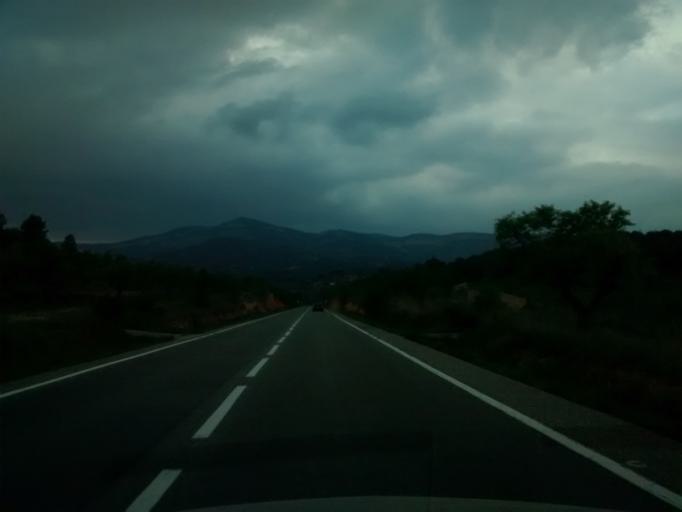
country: ES
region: Catalonia
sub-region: Provincia de Tarragona
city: Benifallet
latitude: 41.0056
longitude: 0.5089
